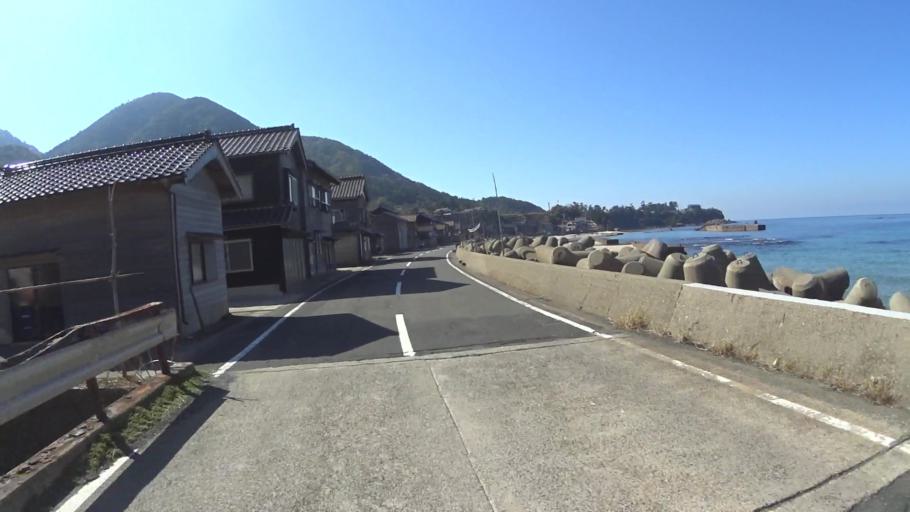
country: JP
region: Kyoto
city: Miyazu
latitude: 35.7636
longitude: 135.2072
